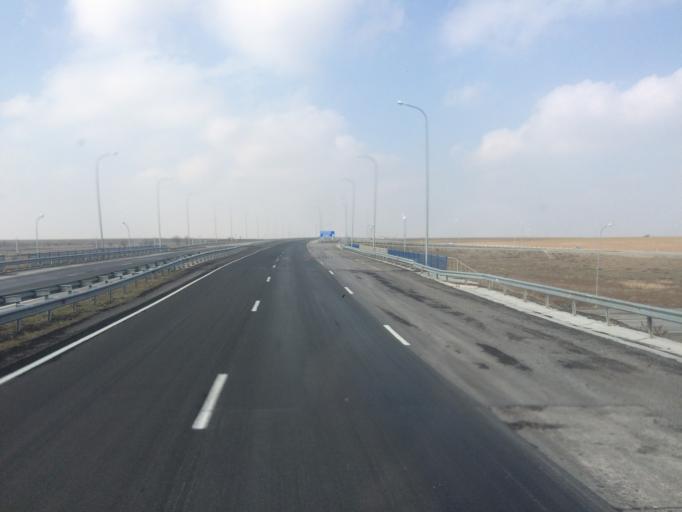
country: KZ
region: Ongtustik Qazaqstan
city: Temirlanovka
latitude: 42.5280
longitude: 69.3466
